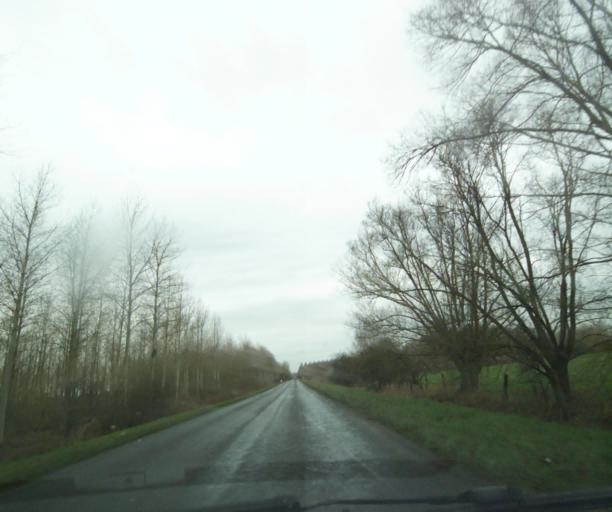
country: FR
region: Nord-Pas-de-Calais
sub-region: Departement du Nord
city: Crespin
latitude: 50.4349
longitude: 3.6298
